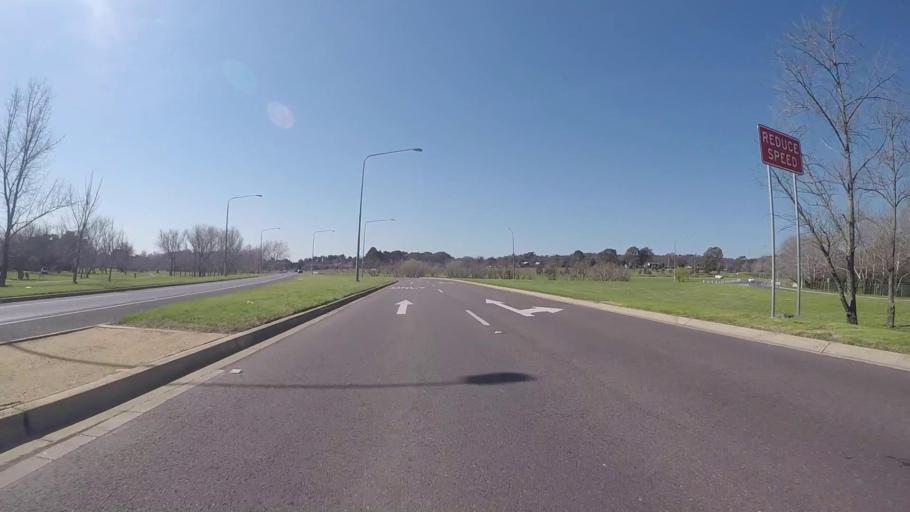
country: AU
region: Australian Capital Territory
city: Forrest
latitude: -35.3370
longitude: 149.0850
